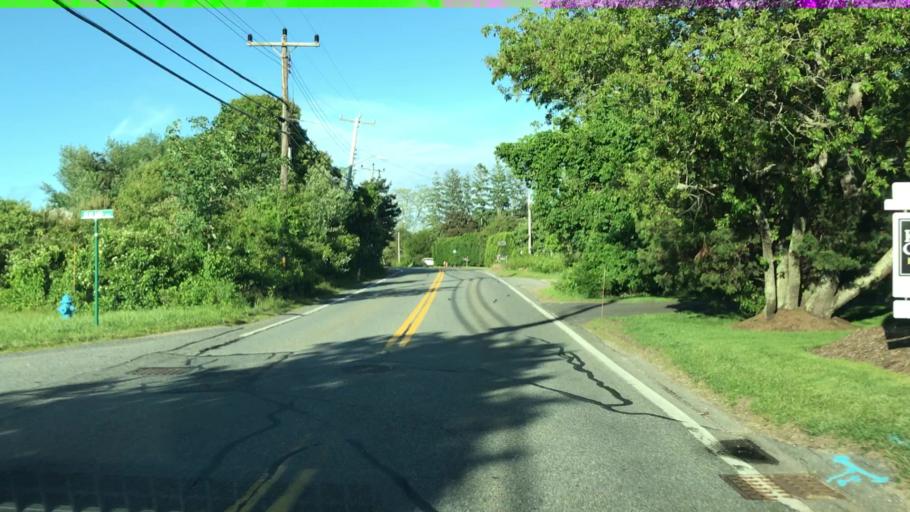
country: US
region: Massachusetts
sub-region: Barnstable County
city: East Harwich
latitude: 41.6999
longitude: -70.0270
